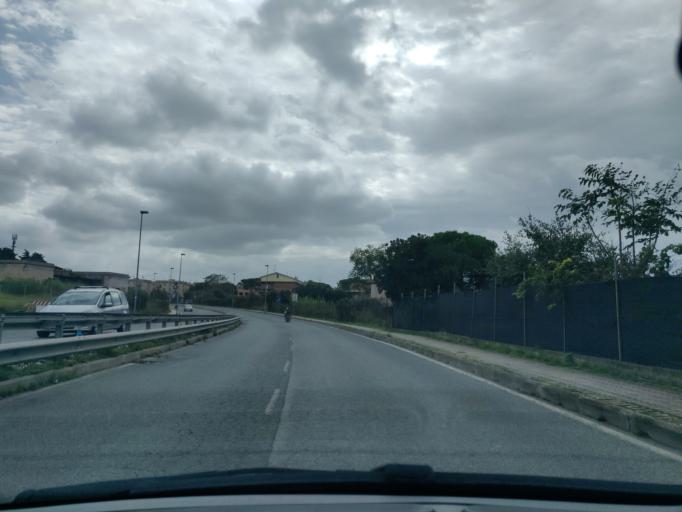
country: IT
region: Latium
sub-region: Citta metropolitana di Roma Capitale
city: Civitavecchia
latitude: 42.1003
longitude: 11.7957
